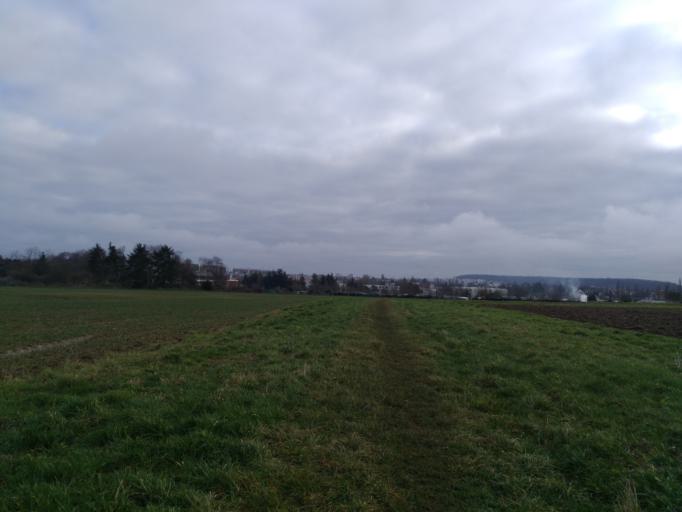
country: FR
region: Ile-de-France
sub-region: Departement des Yvelines
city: Plaisir
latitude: 48.8266
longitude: 1.9324
